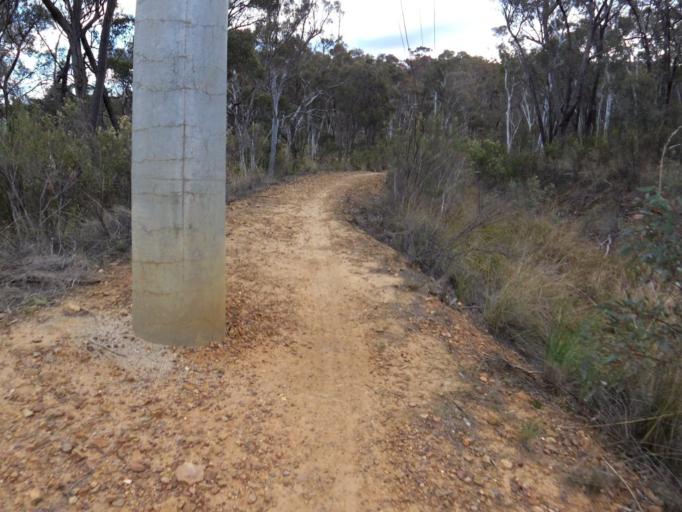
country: AU
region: Australian Capital Territory
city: Acton
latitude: -35.2683
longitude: 149.1091
